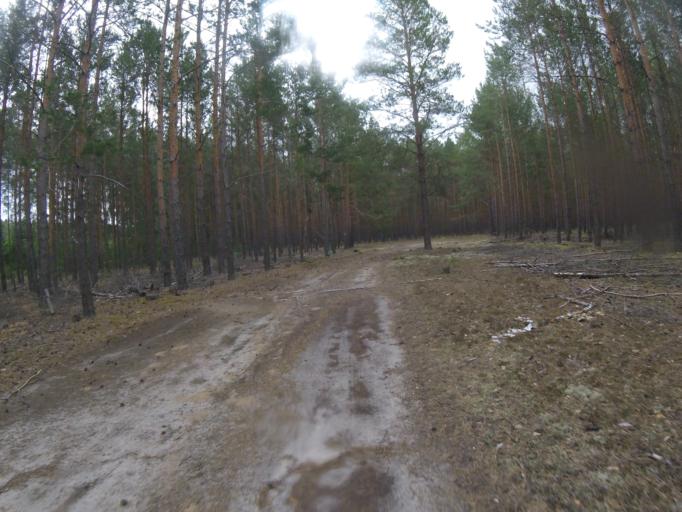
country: DE
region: Brandenburg
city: Gross Koris
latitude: 52.1920
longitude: 13.6547
